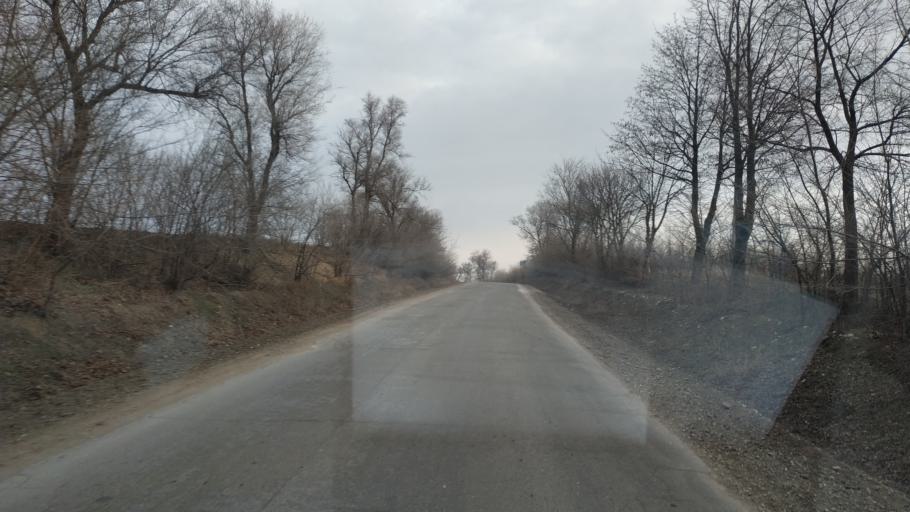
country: MD
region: Chisinau
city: Singera
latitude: 46.9484
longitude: 29.0550
